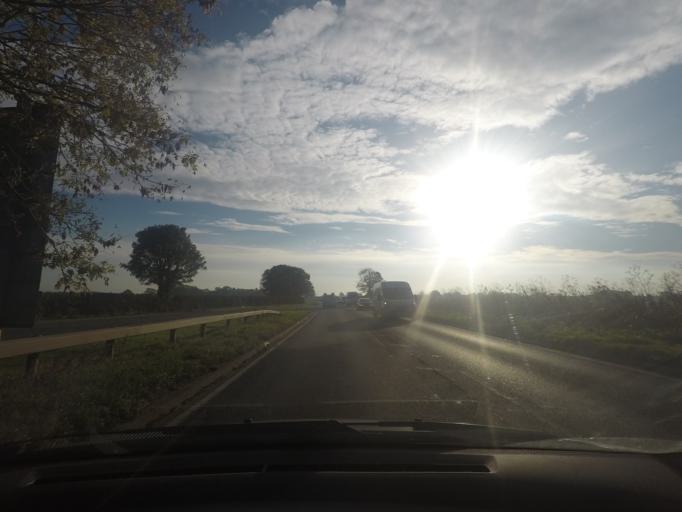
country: GB
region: England
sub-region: City of York
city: Murton
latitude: 53.9560
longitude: -0.9946
